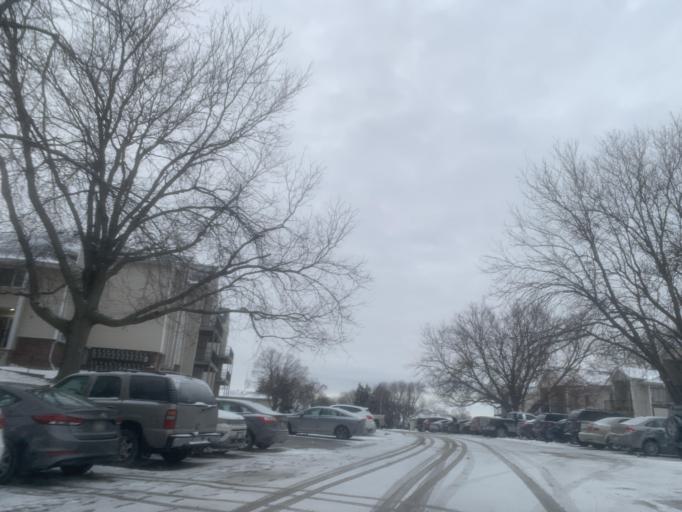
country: US
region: Nebraska
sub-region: Douglas County
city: Ralston
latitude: 41.2722
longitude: -96.0798
